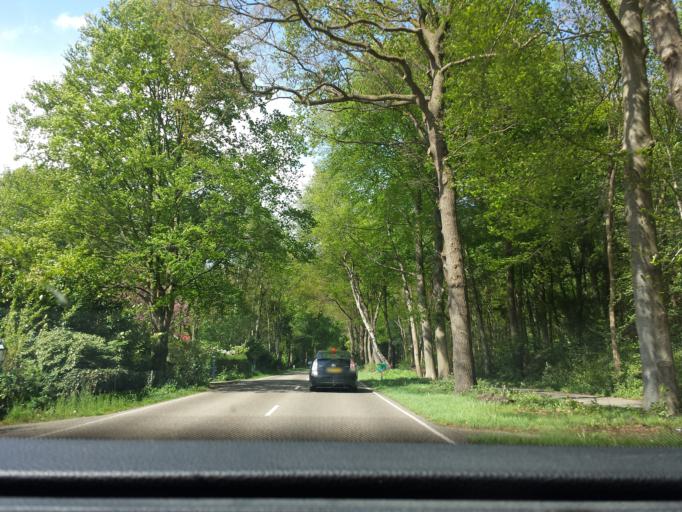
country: NL
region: Gelderland
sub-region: Gemeente Lochem
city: Barchem
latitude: 52.0974
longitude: 6.4498
